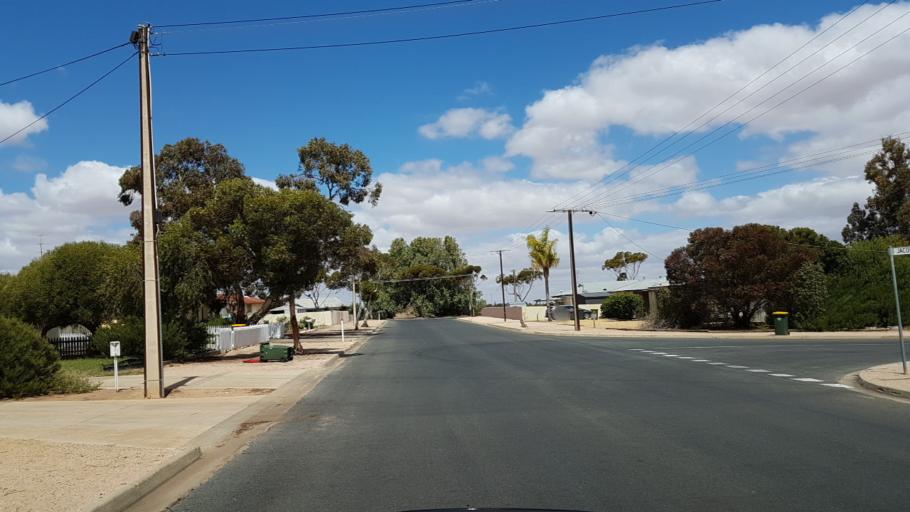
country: AU
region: South Australia
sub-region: Loxton Waikerie
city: Waikerie
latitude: -34.1835
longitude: 139.9903
